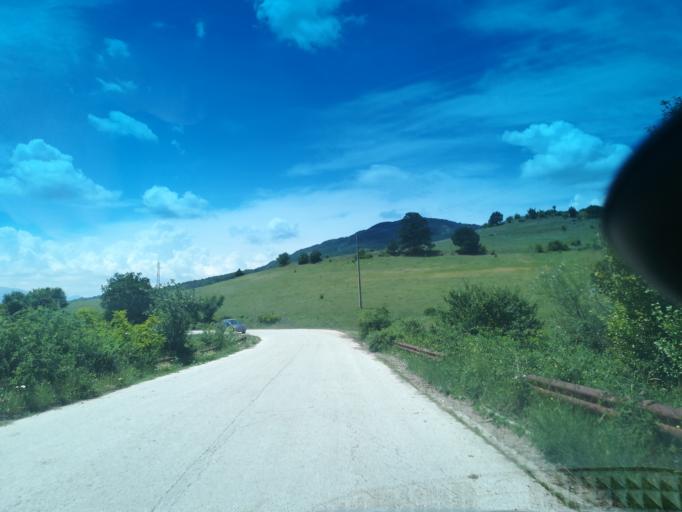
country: BG
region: Khaskovo
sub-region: Obshtina Mineralni Bani
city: Mineralni Bani
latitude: 41.9541
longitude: 25.2532
